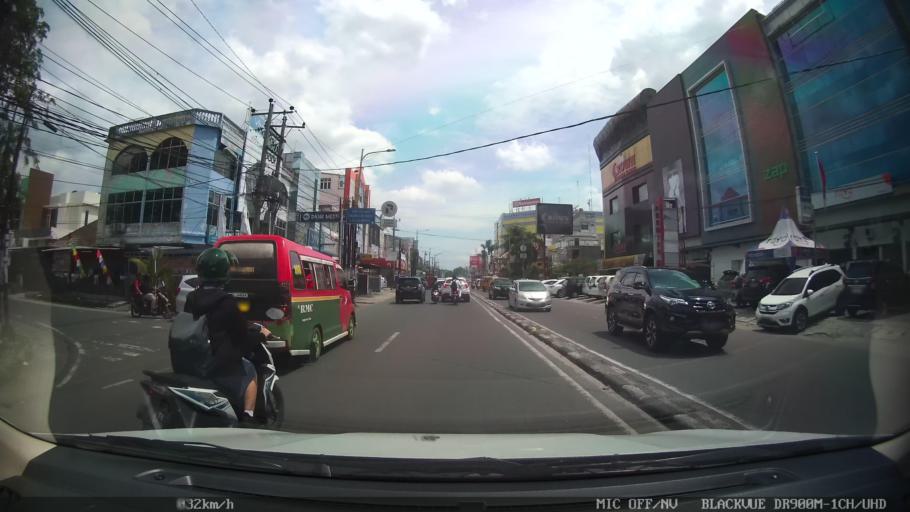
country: ID
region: North Sumatra
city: Medan
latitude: 3.5819
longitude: 98.6612
